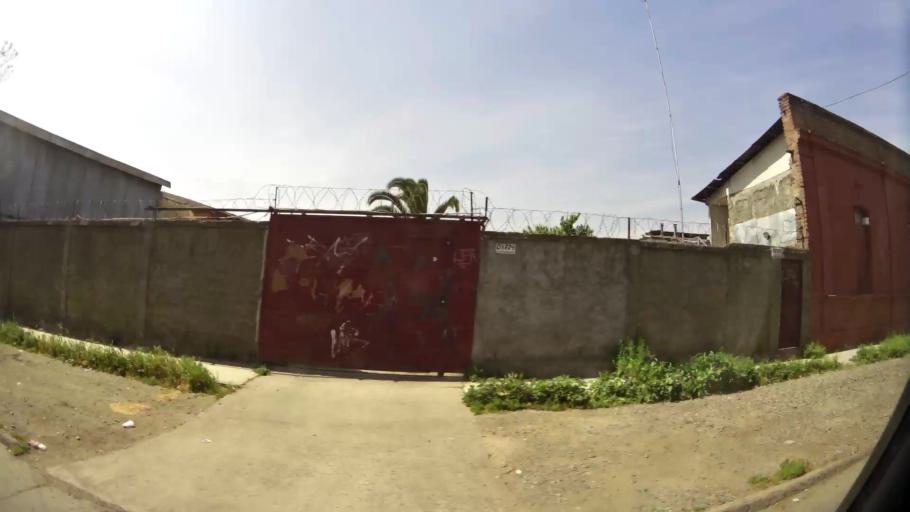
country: CL
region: Santiago Metropolitan
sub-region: Provincia de Santiago
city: Lo Prado
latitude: -33.4300
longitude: -70.6991
